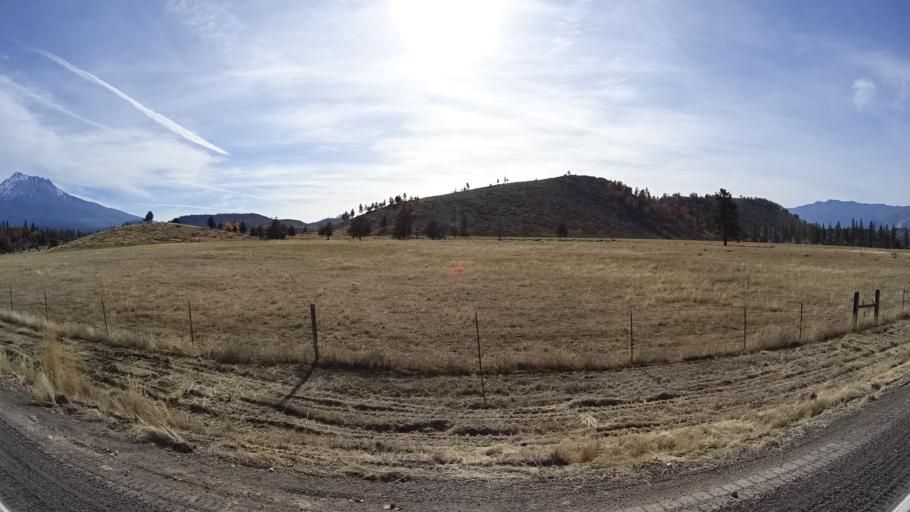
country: US
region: California
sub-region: Siskiyou County
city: Weed
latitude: 41.4941
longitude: -122.3915
